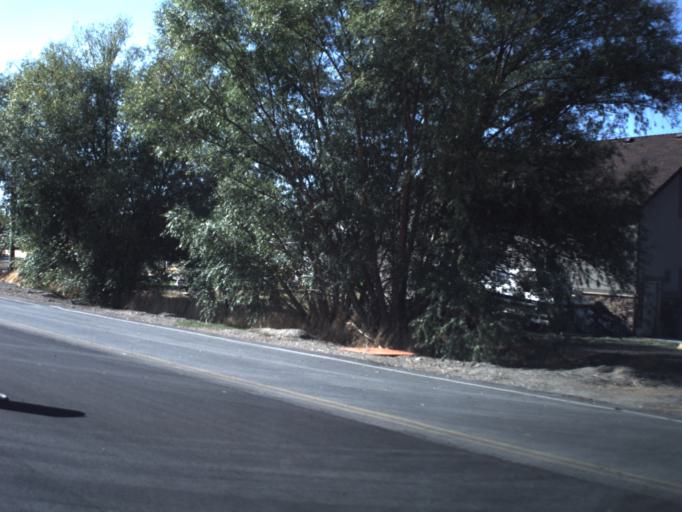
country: US
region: Utah
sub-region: Weber County
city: Hooper
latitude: 41.1908
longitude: -112.1000
